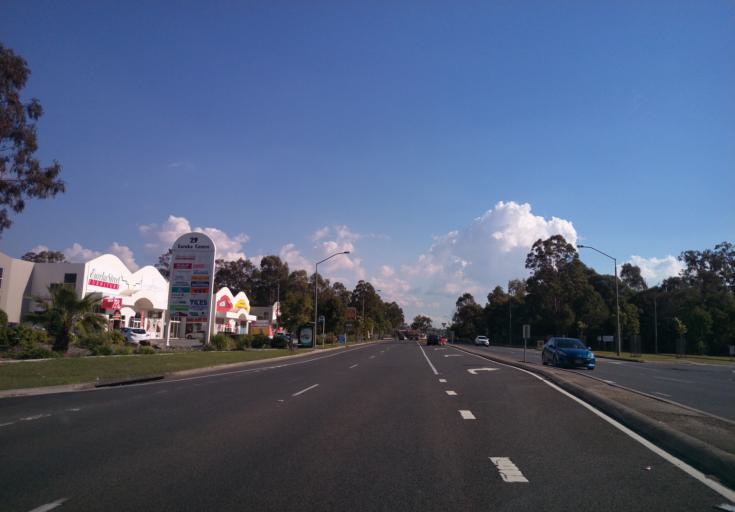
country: AU
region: Queensland
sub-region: Brisbane
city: Chandler
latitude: -27.5231
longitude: 153.1995
